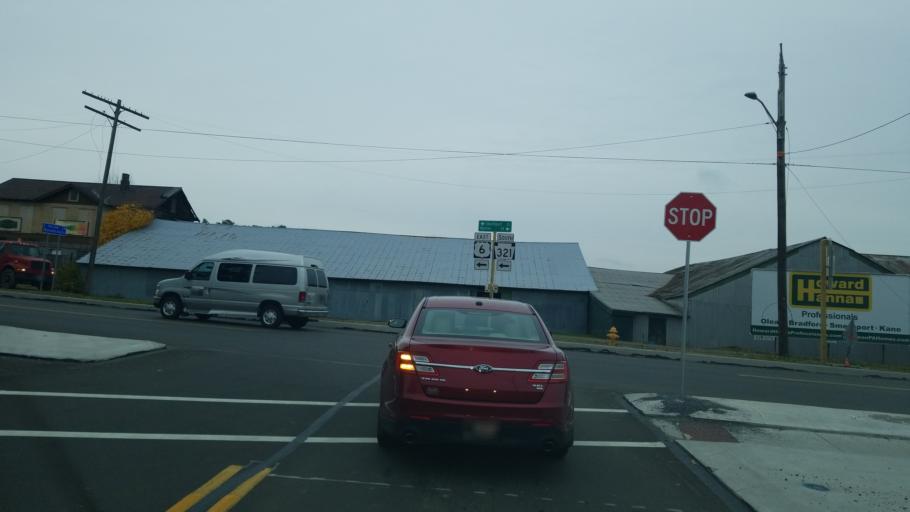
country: US
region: Pennsylvania
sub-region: McKean County
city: Kane
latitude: 41.6601
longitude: -78.8025
